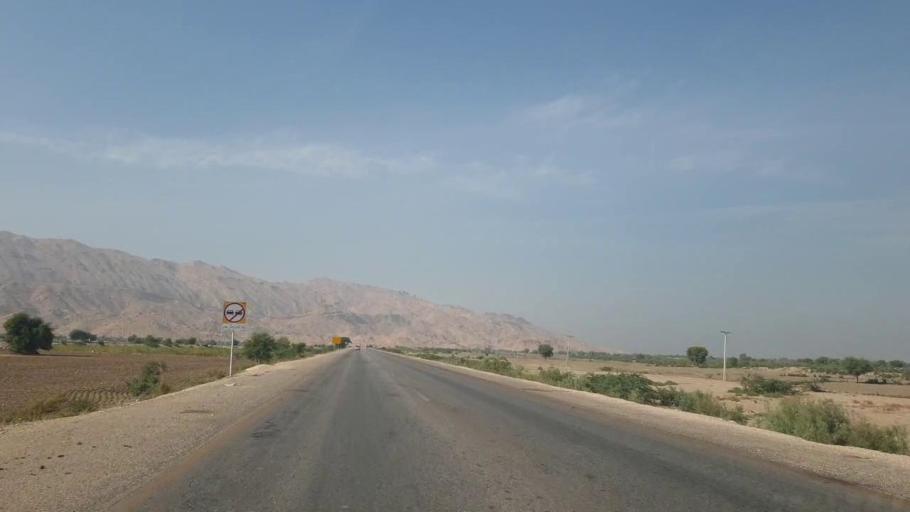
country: PK
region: Sindh
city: Sehwan
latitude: 26.2711
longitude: 67.9023
